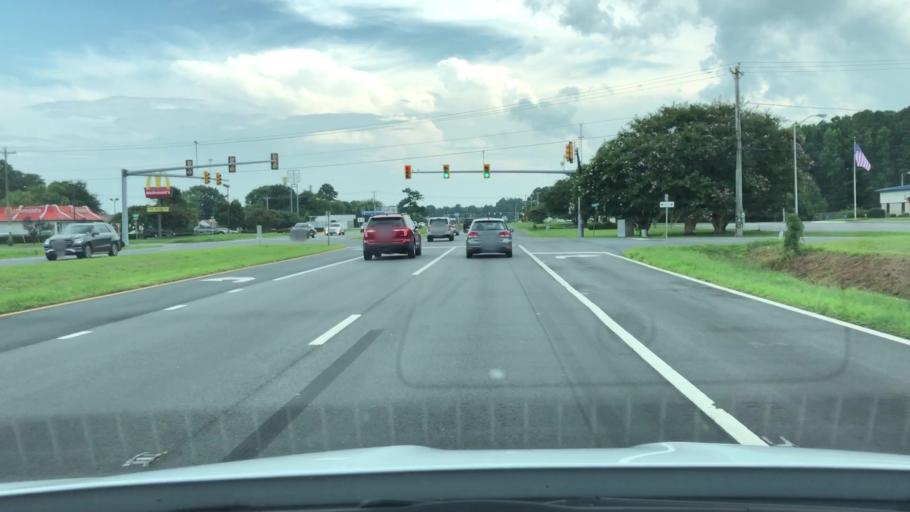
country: US
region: Virginia
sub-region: Northampton County
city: Exmore
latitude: 37.5217
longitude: -75.8320
